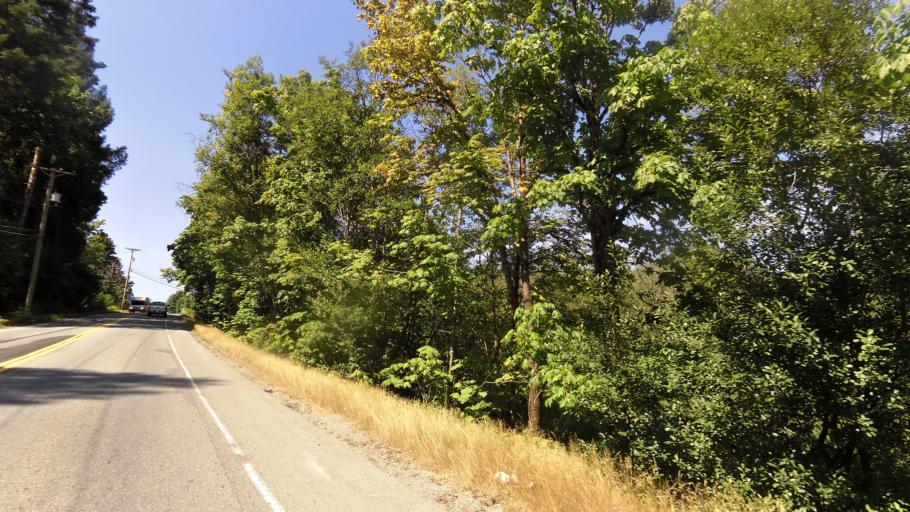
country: CA
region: British Columbia
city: Port Alberni
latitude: 49.2691
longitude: -124.8575
